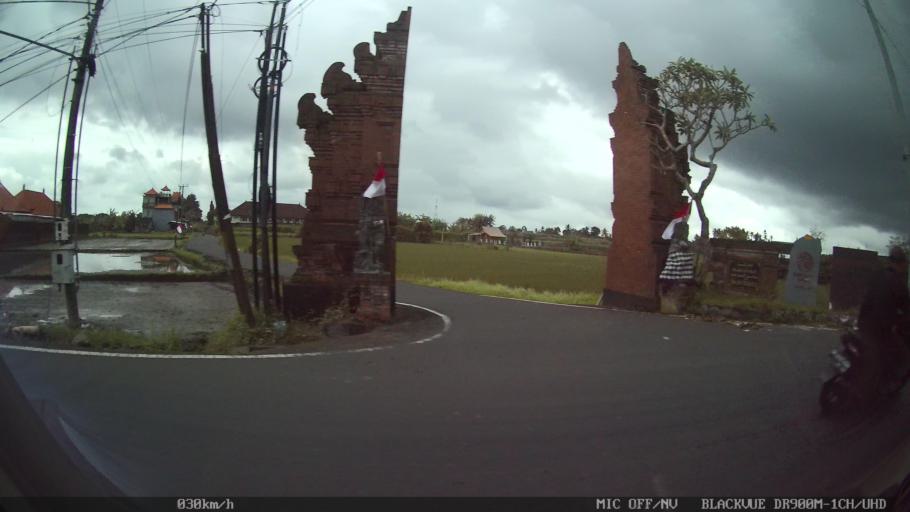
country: ID
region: Bali
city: Banjar Mambalkajanan
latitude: -8.5417
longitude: 115.2227
